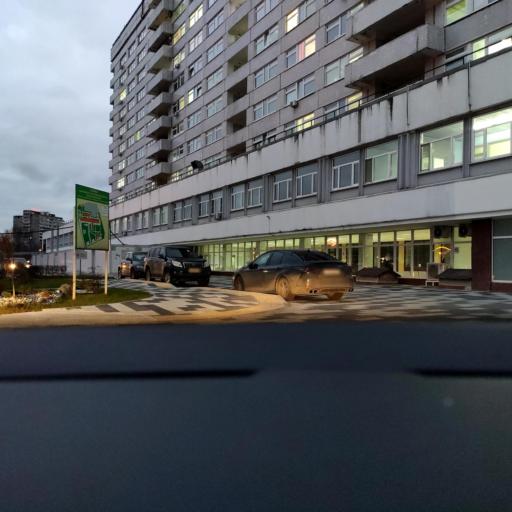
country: RU
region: Moscow
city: Vykhino-Zhulebino
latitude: 55.6902
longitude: 37.8127
